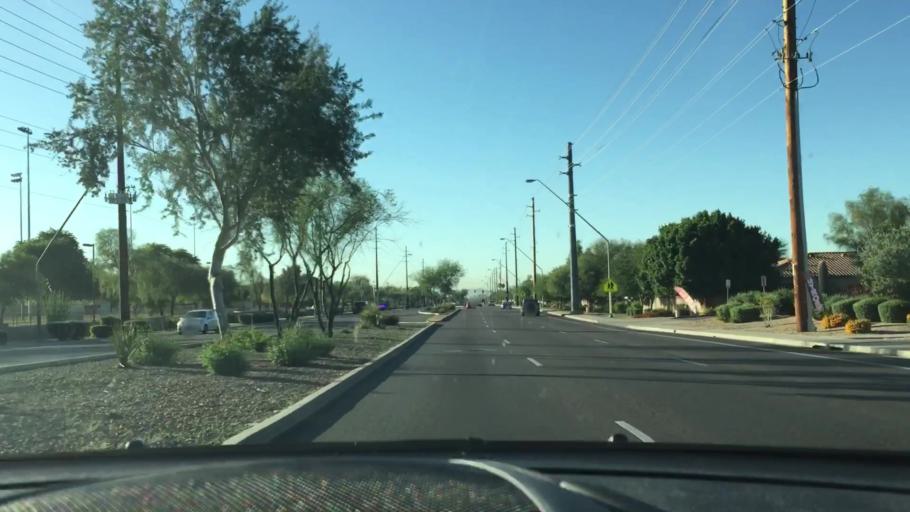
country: US
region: Arizona
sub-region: Maricopa County
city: Gilbert
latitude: 33.4359
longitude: -111.6844
